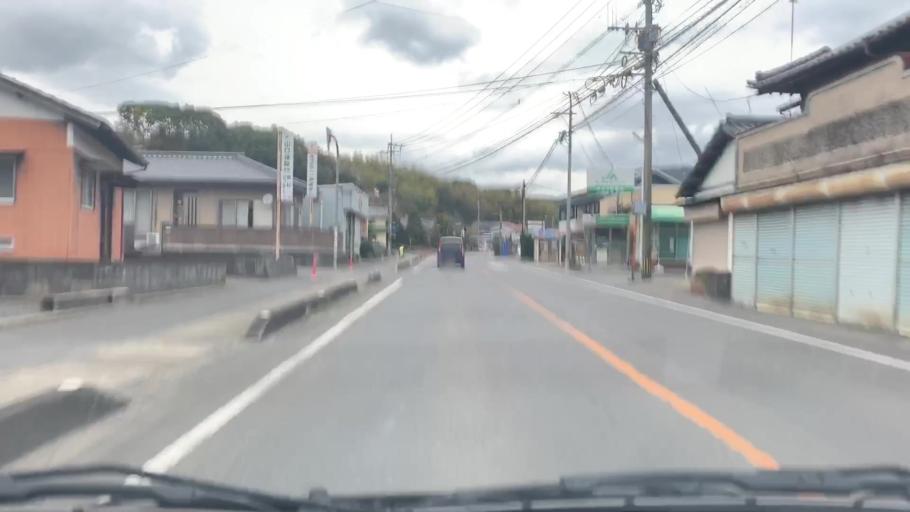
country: JP
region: Saga Prefecture
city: Kashima
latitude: 33.1478
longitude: 130.0630
